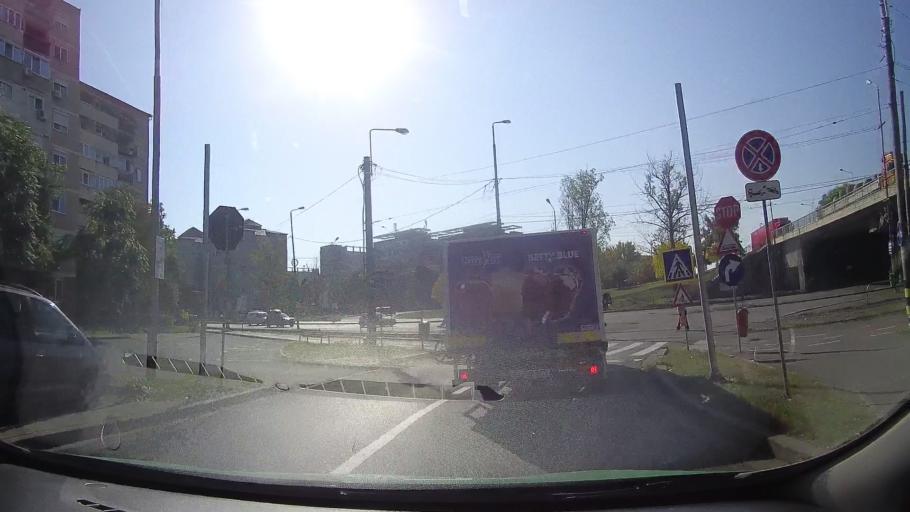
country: RO
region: Bihor
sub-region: Comuna Biharea
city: Oradea
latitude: 47.0747
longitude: 21.9080
